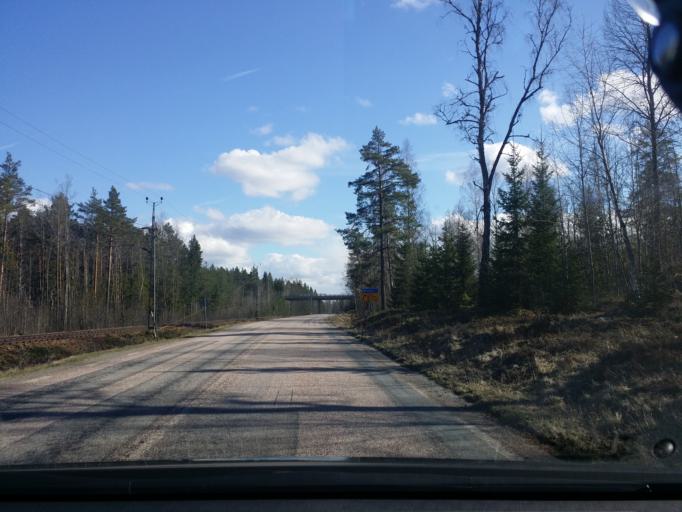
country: SE
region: Vaestmanland
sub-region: Sala Kommun
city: Sala
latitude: 59.9710
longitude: 16.5025
